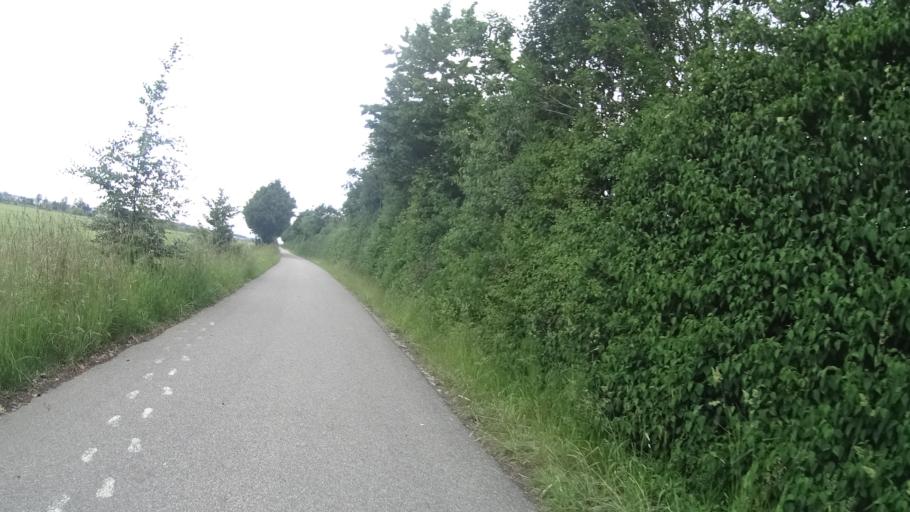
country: DE
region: Bavaria
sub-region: Lower Bavaria
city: Eggenfelden
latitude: 48.3972
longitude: 12.7486
